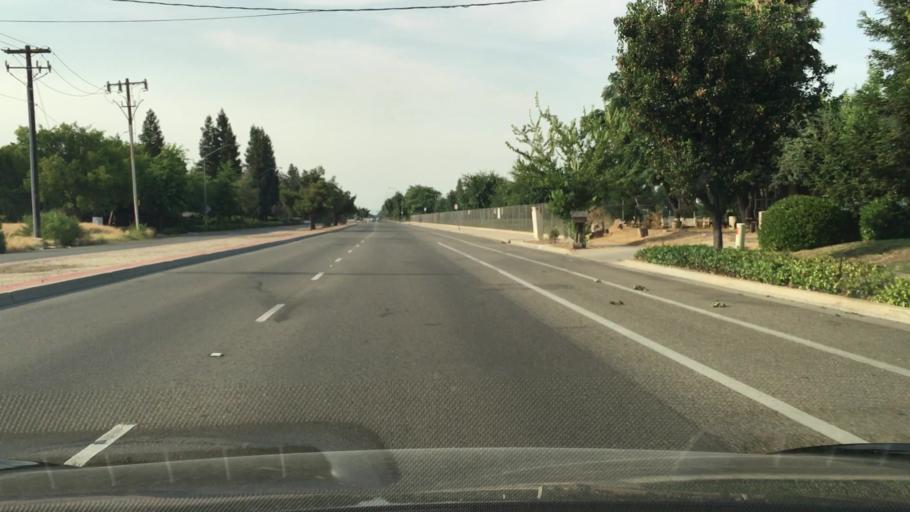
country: US
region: California
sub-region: Fresno County
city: Clovis
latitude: 36.8460
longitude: -119.7387
